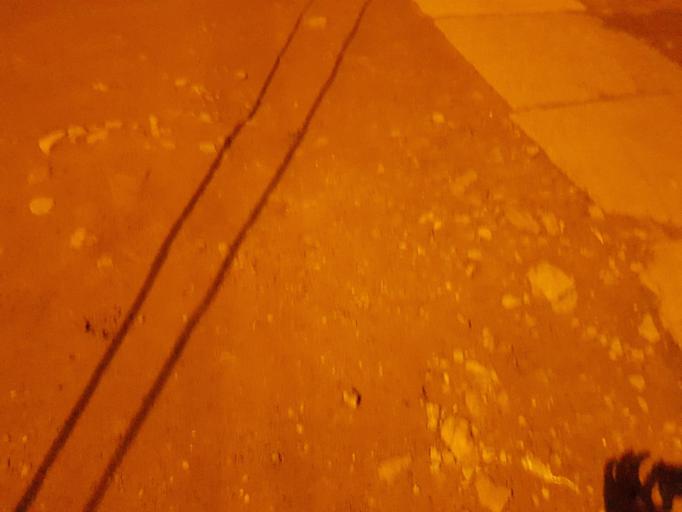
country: ML
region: Bamako
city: Bamako
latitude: 12.5862
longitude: -7.9507
